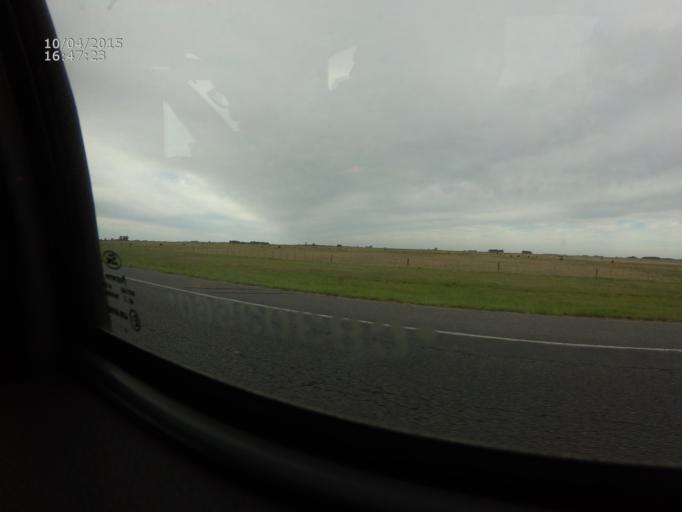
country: AR
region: Buenos Aires
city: Coronel Vidal
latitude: -37.6758
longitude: -57.6647
